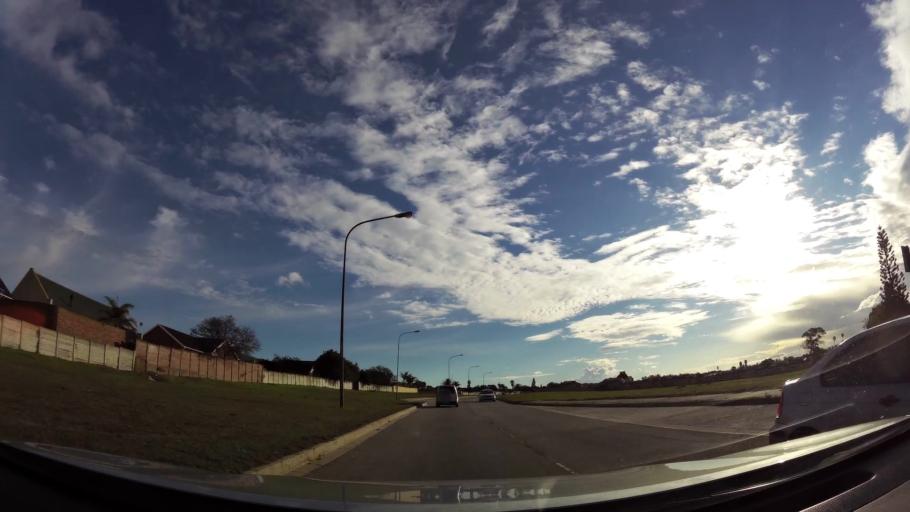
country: ZA
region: Eastern Cape
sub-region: Nelson Mandela Bay Metropolitan Municipality
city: Port Elizabeth
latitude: -33.9600
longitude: 25.4840
